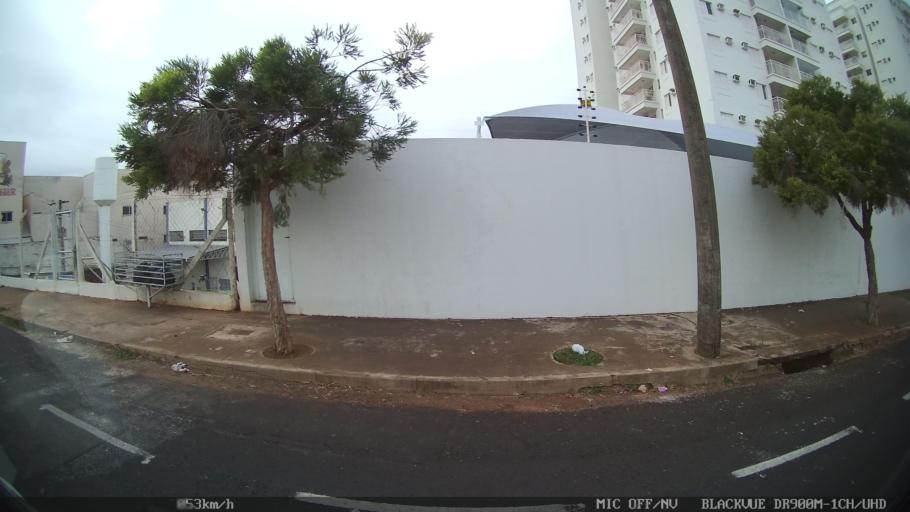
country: BR
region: Sao Paulo
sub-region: Sao Jose Do Rio Preto
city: Sao Jose do Rio Preto
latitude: -20.8392
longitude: -49.3955
